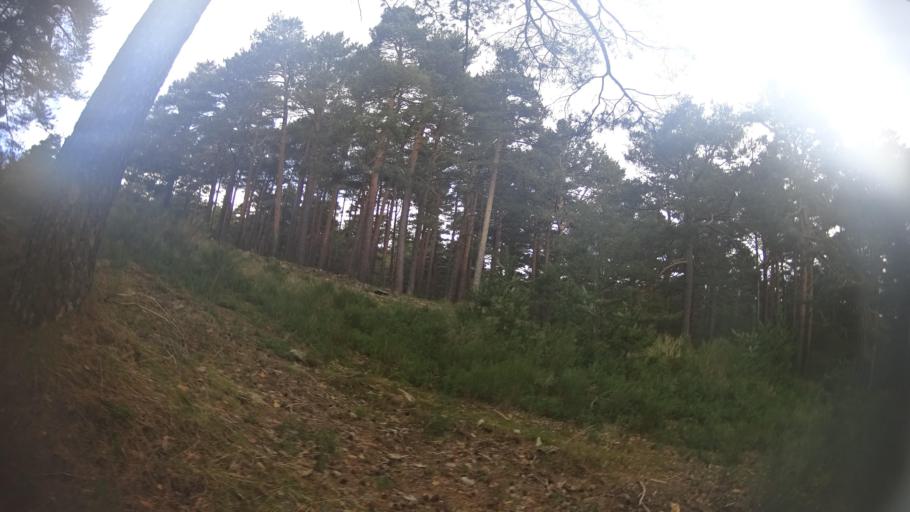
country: ES
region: Madrid
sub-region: Provincia de Madrid
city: Miraflores de la Sierra
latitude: 40.8690
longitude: -3.7899
